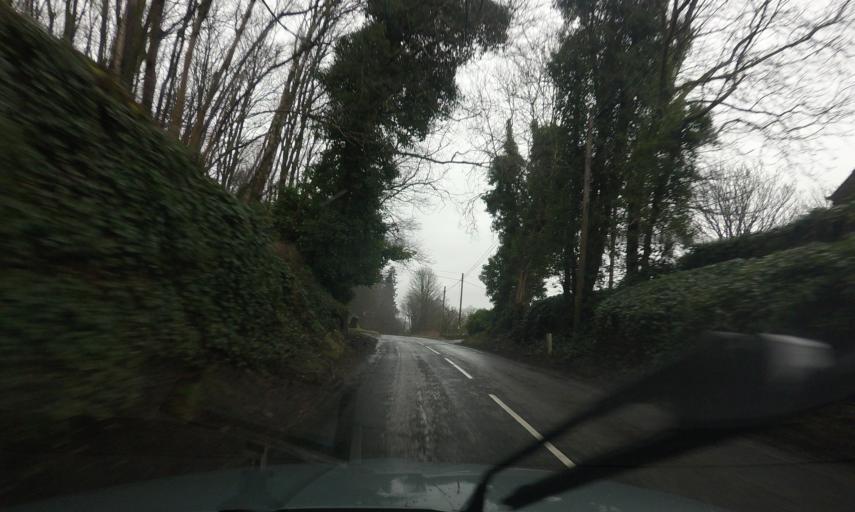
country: GB
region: Scotland
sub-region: Stirling
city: Balfron
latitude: 56.1541
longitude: -4.3625
